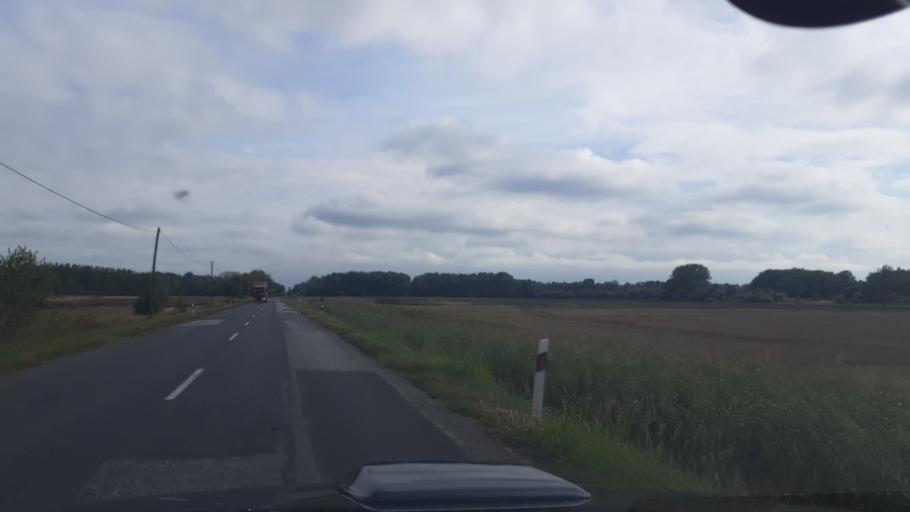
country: HU
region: Bacs-Kiskun
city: Fulopszallas
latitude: 46.8023
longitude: 19.1473
